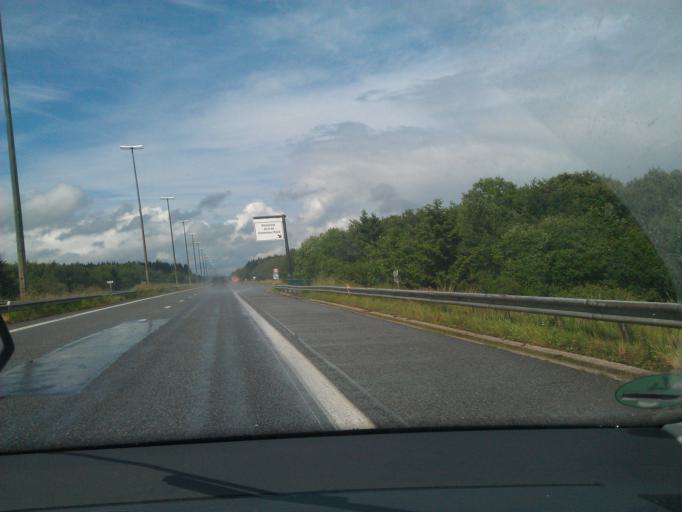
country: BE
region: Wallonia
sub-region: Province de Liege
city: Saint-Vith
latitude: 50.3125
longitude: 6.0826
